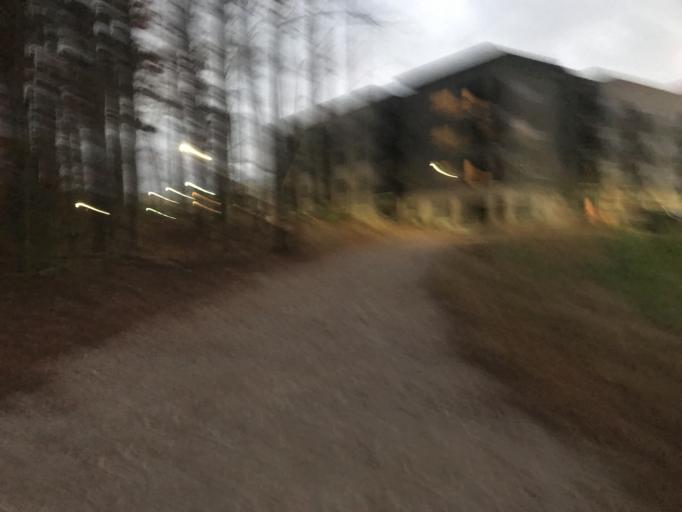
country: US
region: North Carolina
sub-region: Wake County
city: West Raleigh
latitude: 35.8344
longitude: -78.6643
